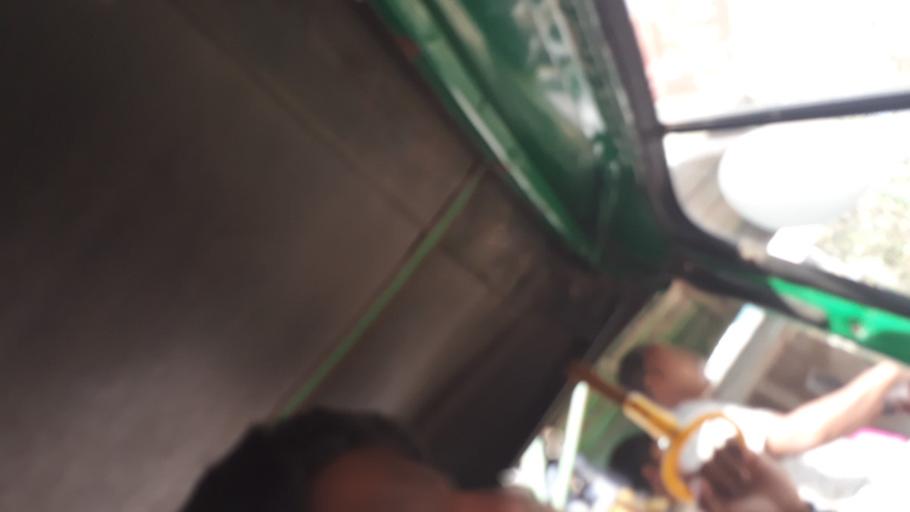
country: BD
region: Khulna
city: Kushtia
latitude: 23.8630
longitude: 89.0353
